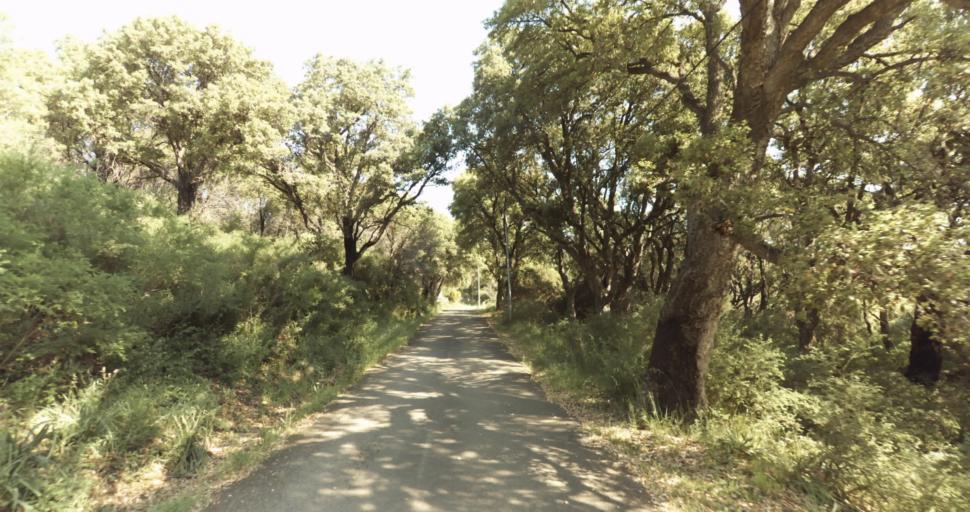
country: FR
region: Corsica
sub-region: Departement de la Haute-Corse
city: Furiani
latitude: 42.6378
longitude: 9.4164
